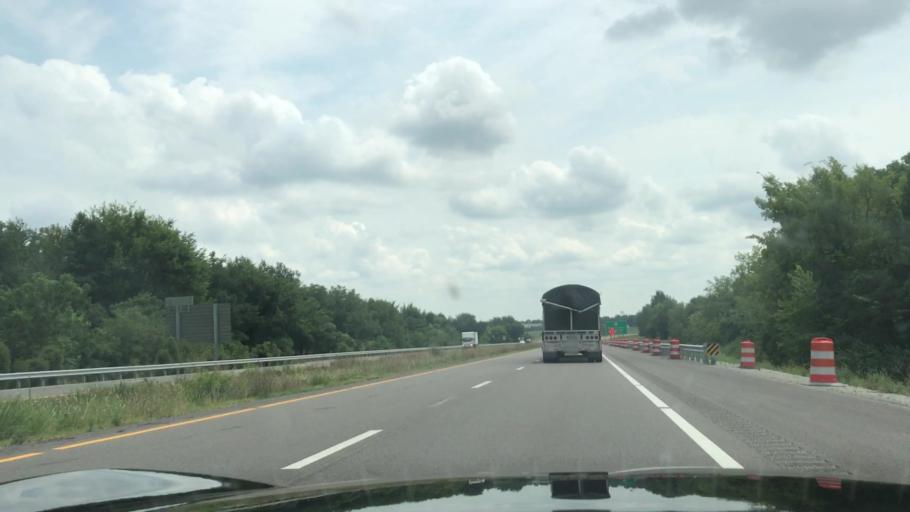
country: US
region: Kentucky
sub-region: Warren County
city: Bowling Green
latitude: 36.9656
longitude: -86.4988
